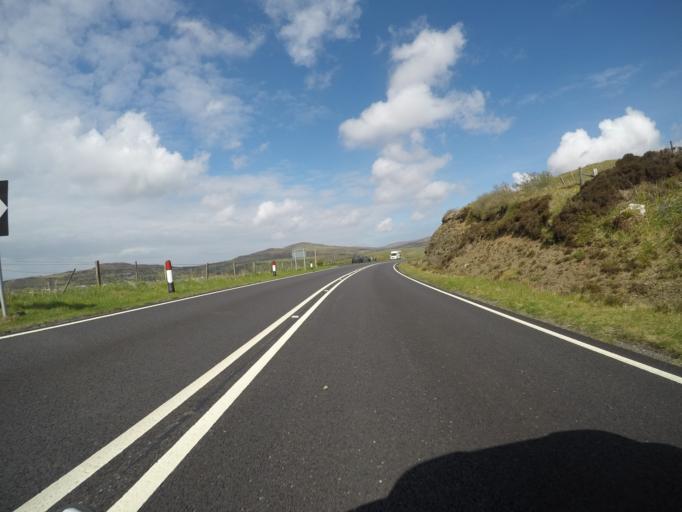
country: GB
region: Scotland
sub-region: Highland
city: Portree
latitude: 57.5774
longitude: -6.3652
